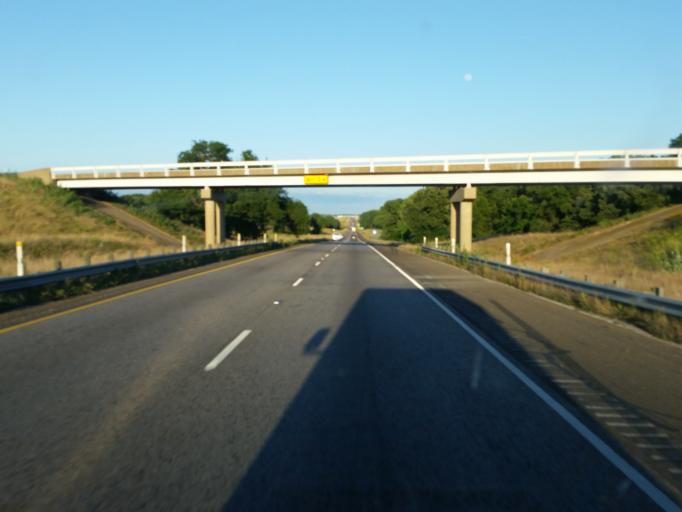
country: US
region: Texas
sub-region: Van Zandt County
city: Wills Point
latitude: 32.6639
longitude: -96.1281
